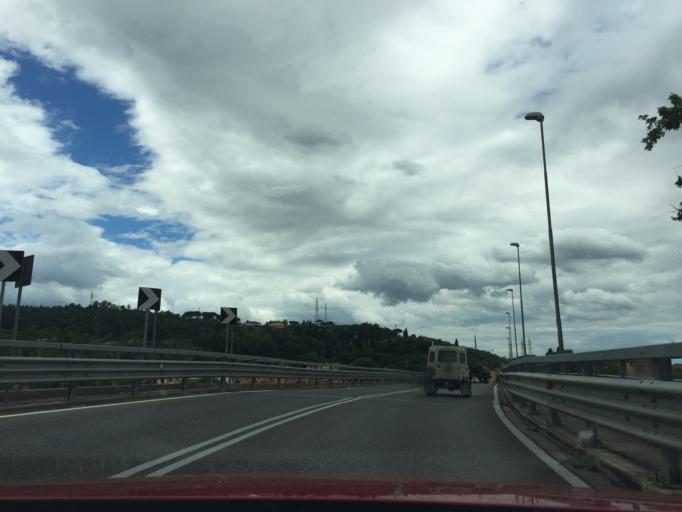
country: IT
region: Tuscany
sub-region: Province of Florence
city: Montelupo Fiorentino
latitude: 43.7275
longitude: 11.0263
